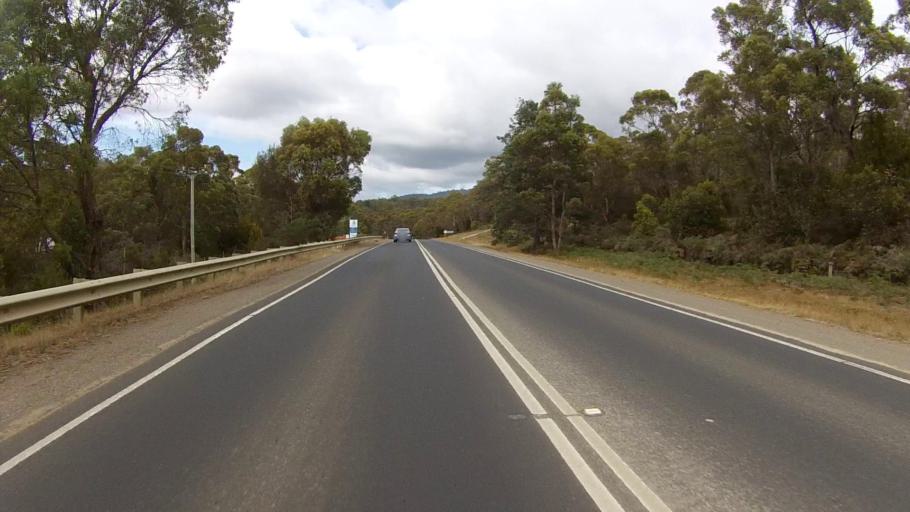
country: AU
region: Tasmania
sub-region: Kingborough
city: Margate
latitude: -43.0471
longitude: 147.2641
